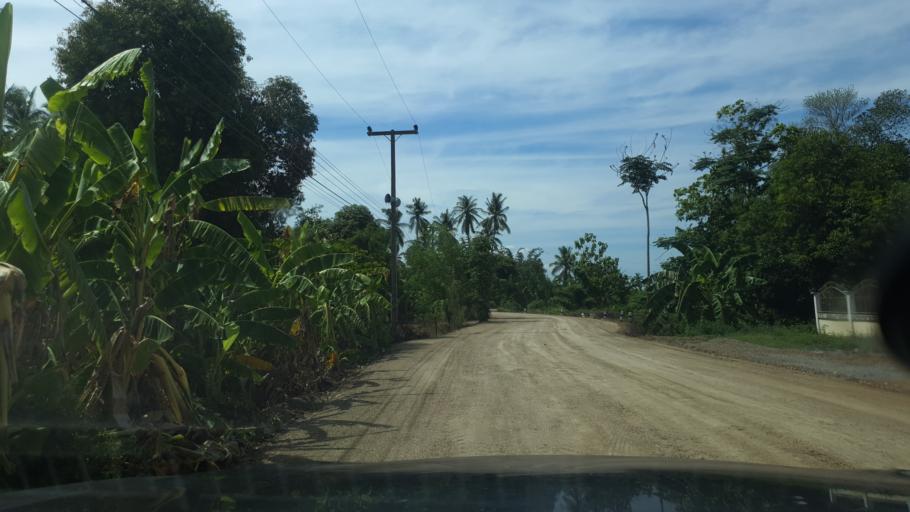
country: TH
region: Sukhothai
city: Si Samrong
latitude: 17.2113
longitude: 99.7189
